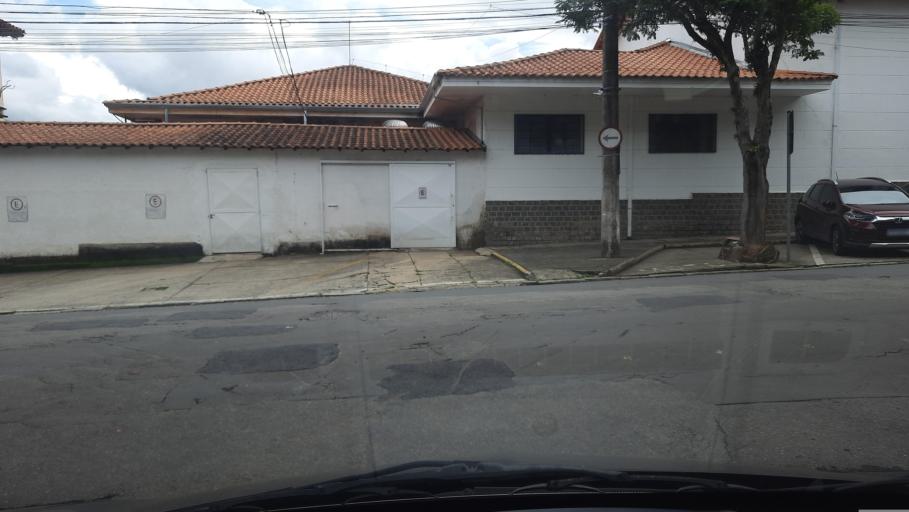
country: BR
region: Minas Gerais
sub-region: Pocos De Caldas
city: Pocos de Caldas
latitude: -21.7800
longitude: -46.5666
